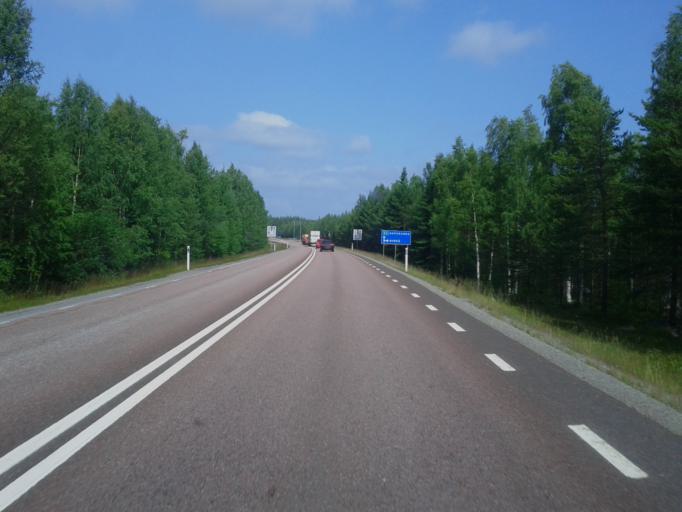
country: SE
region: Vaesterbotten
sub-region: Skelleftea Kommun
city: Burea
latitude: 64.6274
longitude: 21.1781
